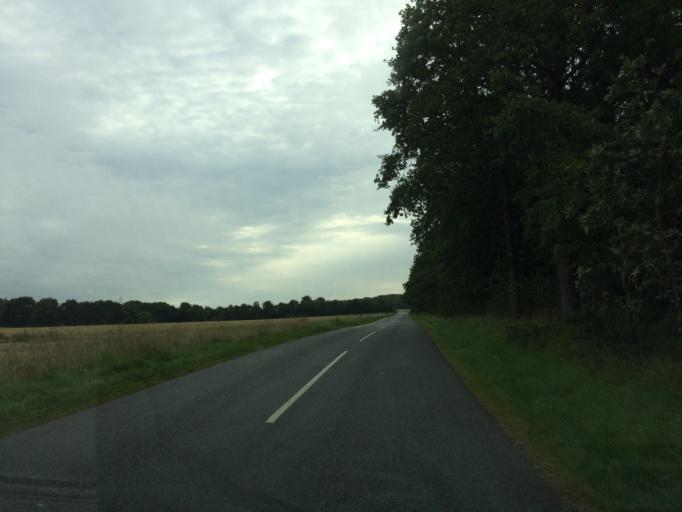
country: DK
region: Central Jutland
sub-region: Herning Kommune
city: Lind
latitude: 56.0918
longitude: 8.9630
